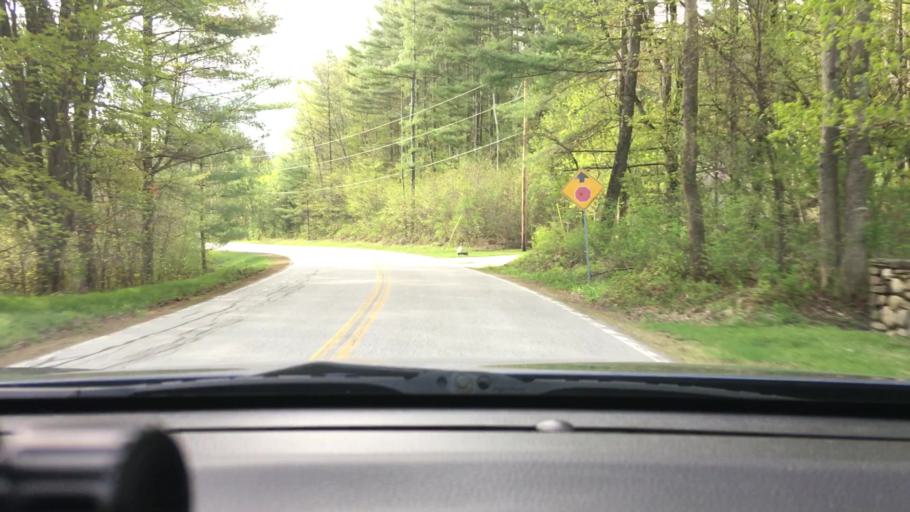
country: US
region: Vermont
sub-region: Bennington County
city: Manchester Center
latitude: 43.2196
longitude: -73.0730
